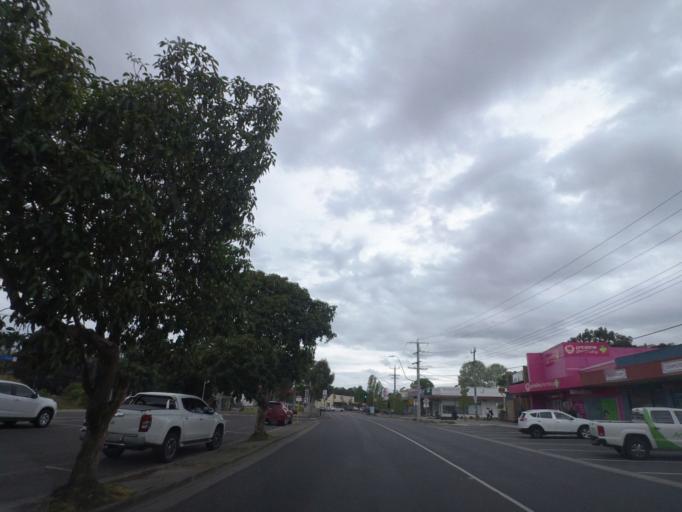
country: AU
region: Victoria
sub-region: Maroondah
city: Croydon North
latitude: -37.7851
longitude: 145.3116
